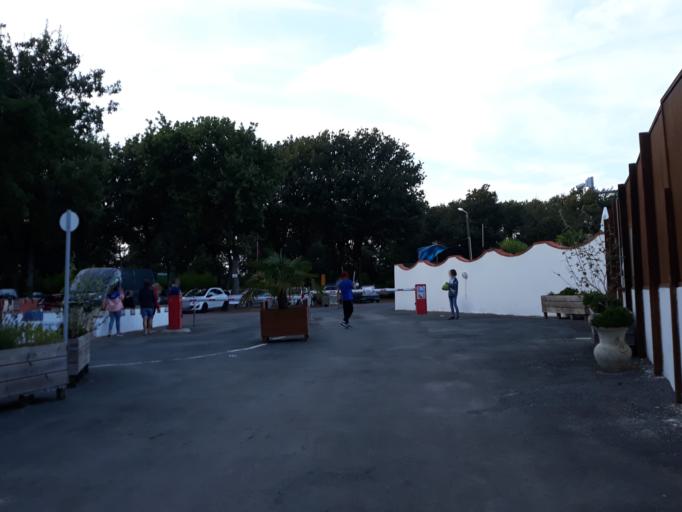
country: FR
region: Poitou-Charentes
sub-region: Departement de la Charente-Maritime
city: Saint-Laurent-de-la-Pree
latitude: 45.9894
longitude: -1.0522
